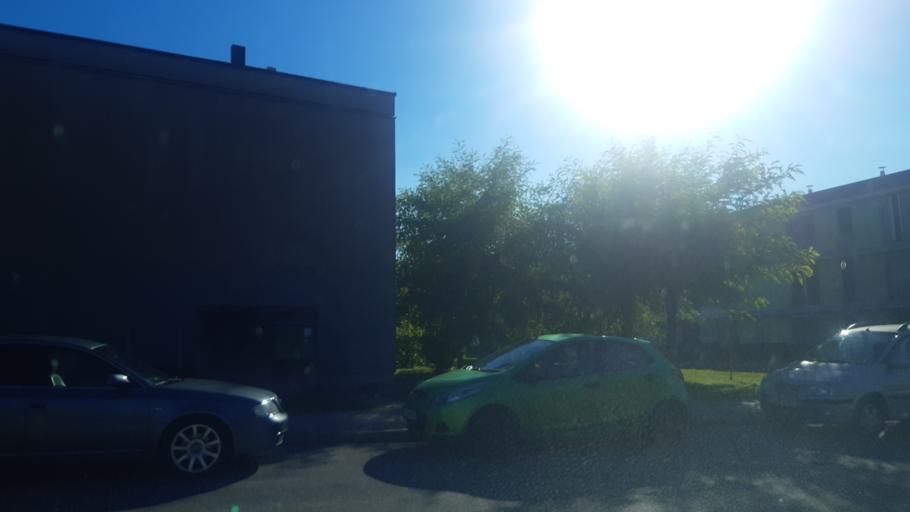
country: SI
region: Ljubljana
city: Ljubljana
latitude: 46.0681
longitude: 14.4734
